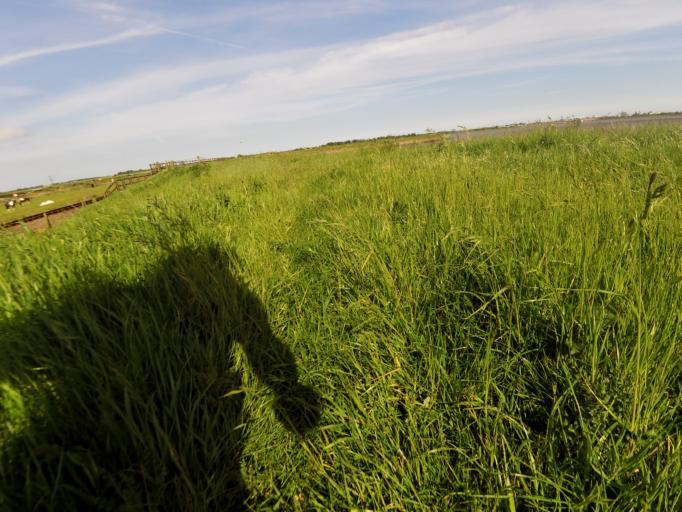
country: GB
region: England
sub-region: Norfolk
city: Great Yarmouth
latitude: 52.6179
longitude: 1.6943
